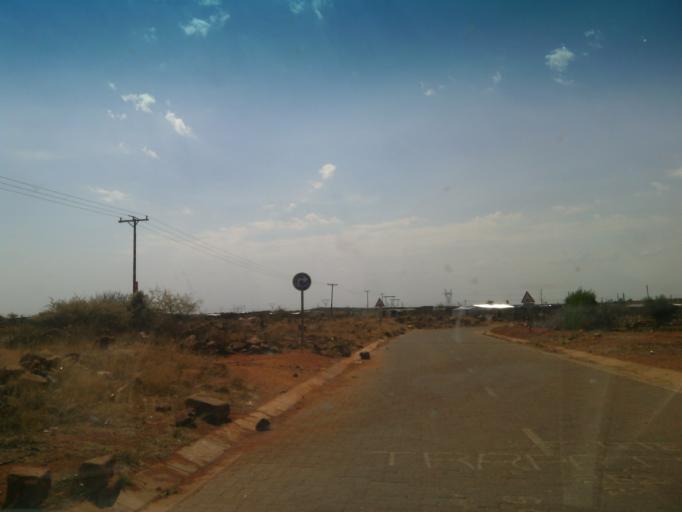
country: ZA
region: Northern Cape
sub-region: Frances Baard District Municipality
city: Barkly West
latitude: -28.5222
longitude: 24.4986
